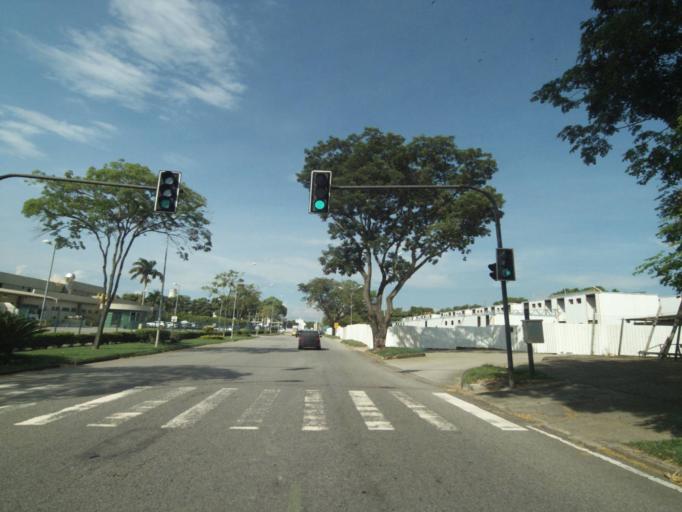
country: BR
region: Rio de Janeiro
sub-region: Rio De Janeiro
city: Rio de Janeiro
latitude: -22.8557
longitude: -43.2329
